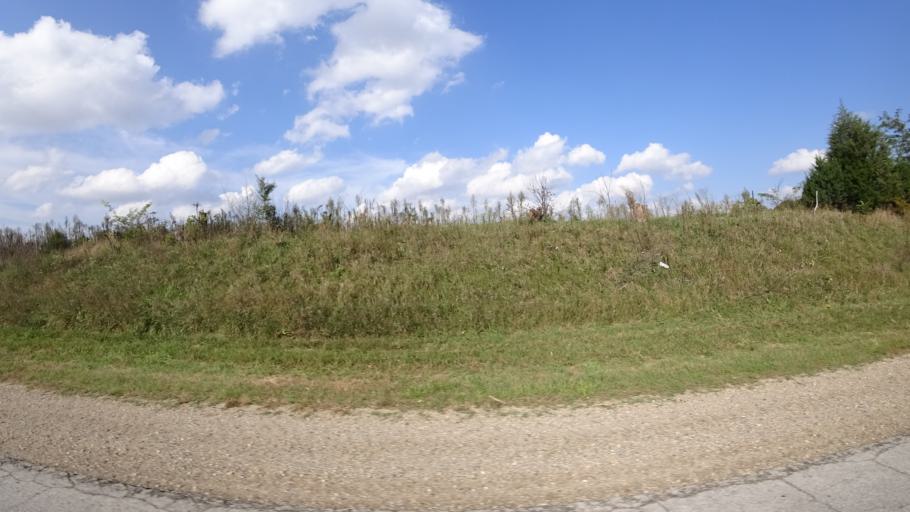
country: US
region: Michigan
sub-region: Saint Joseph County
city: Colon
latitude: 42.0102
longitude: -85.3903
